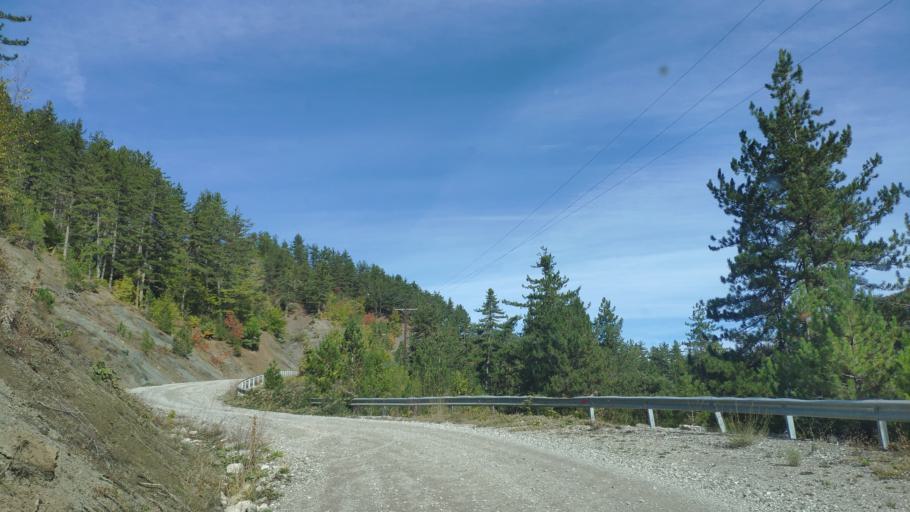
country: AL
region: Korce
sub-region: Rrethi i Devollit
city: Miras
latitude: 40.4162
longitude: 20.8707
